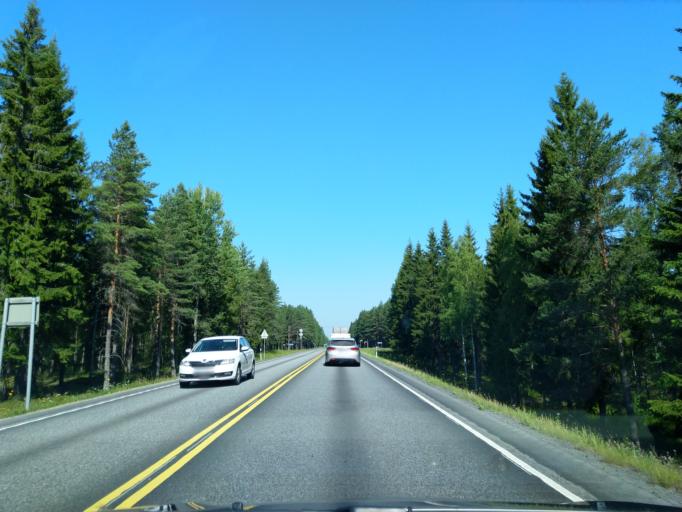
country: FI
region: Satakunta
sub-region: Pori
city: Huittinen
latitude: 61.1232
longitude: 22.8113
